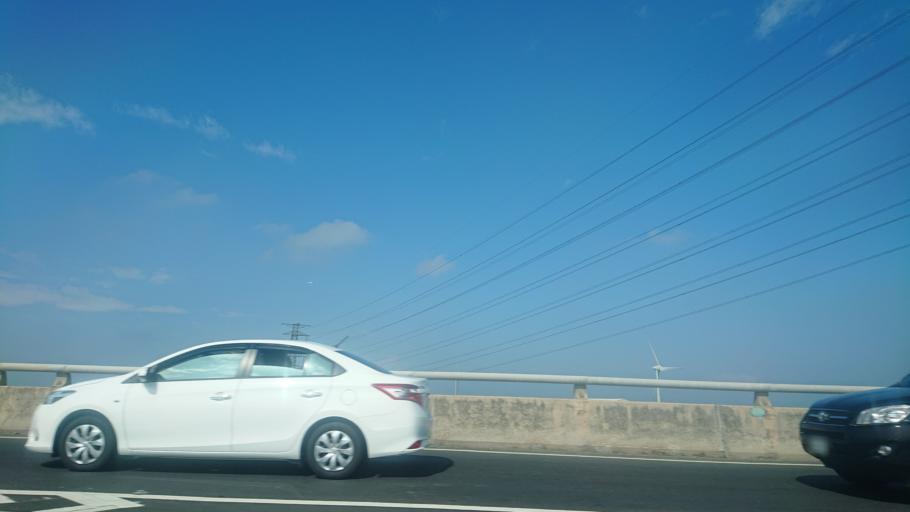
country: TW
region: Taiwan
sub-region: Changhua
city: Chang-hua
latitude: 24.0804
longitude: 120.4187
